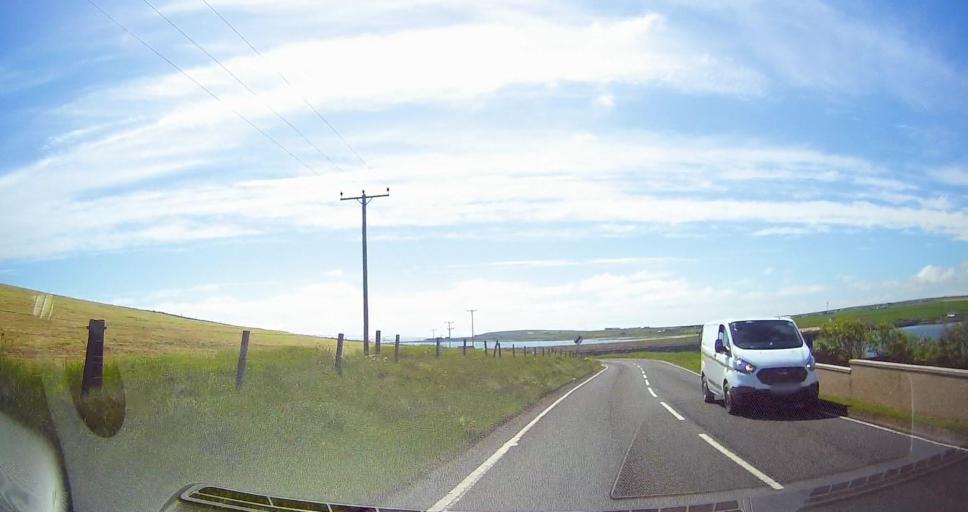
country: GB
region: Scotland
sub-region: Orkney Islands
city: Kirkwall
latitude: 58.8457
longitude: -2.9047
